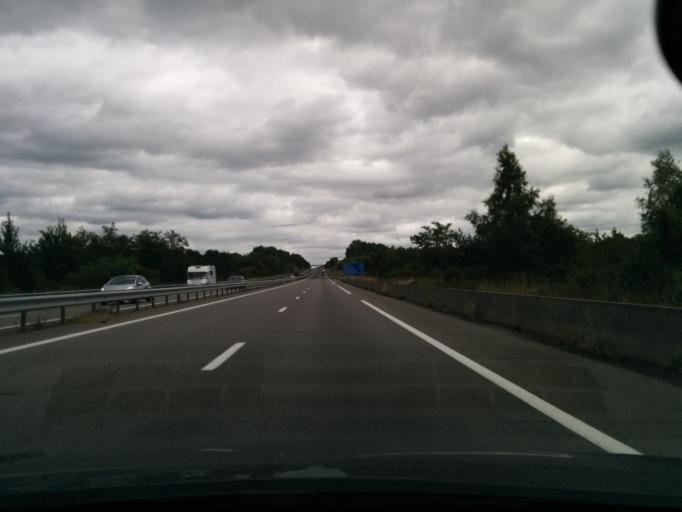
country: FR
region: Limousin
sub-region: Departement de la Haute-Vienne
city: Saint-Sulpice-les-Feuilles
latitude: 46.3635
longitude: 1.4342
